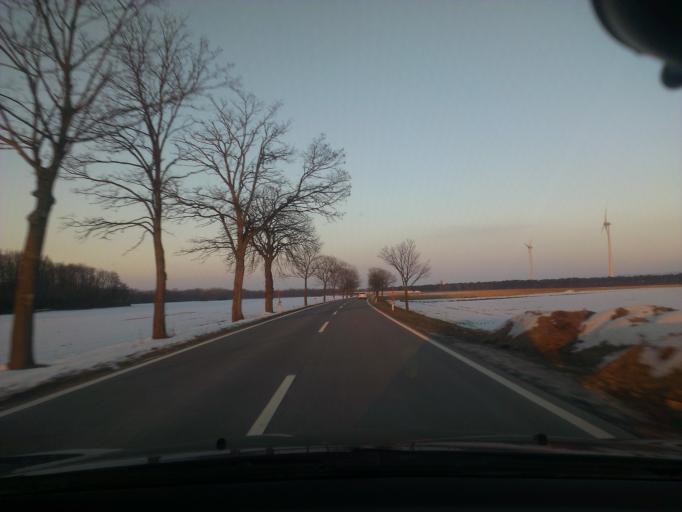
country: AT
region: Lower Austria
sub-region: Politischer Bezirk Baden
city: Mitterndorf an der Fischa
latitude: 47.9643
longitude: 16.4722
